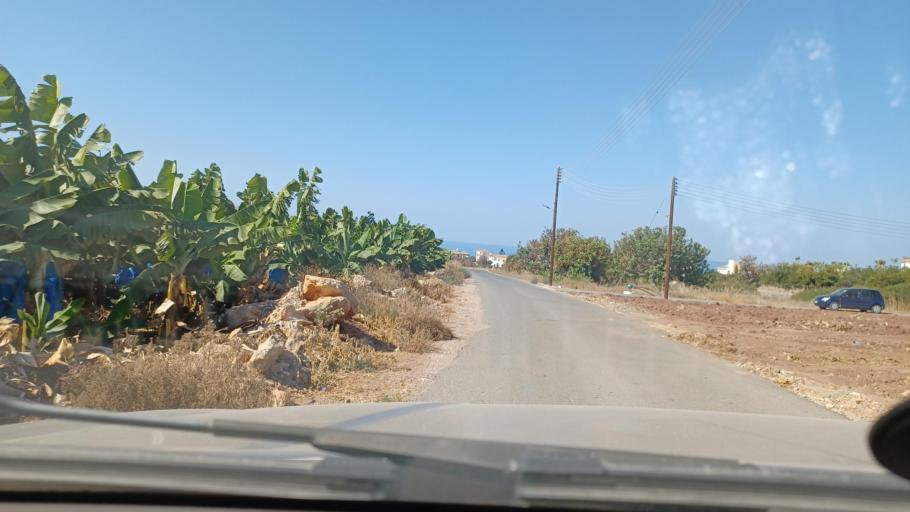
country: CY
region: Pafos
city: Pegeia
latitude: 34.9020
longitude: 32.3345
